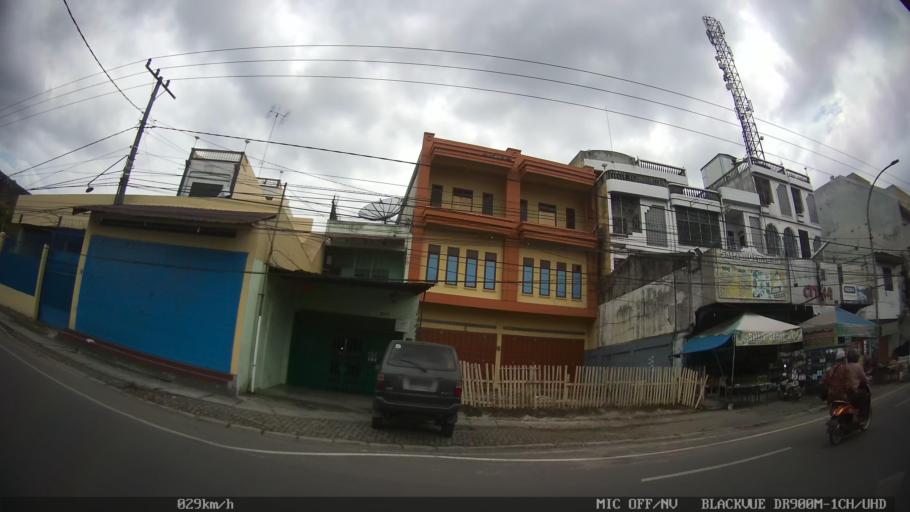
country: ID
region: North Sumatra
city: Sunggal
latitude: 3.5973
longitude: 98.6103
